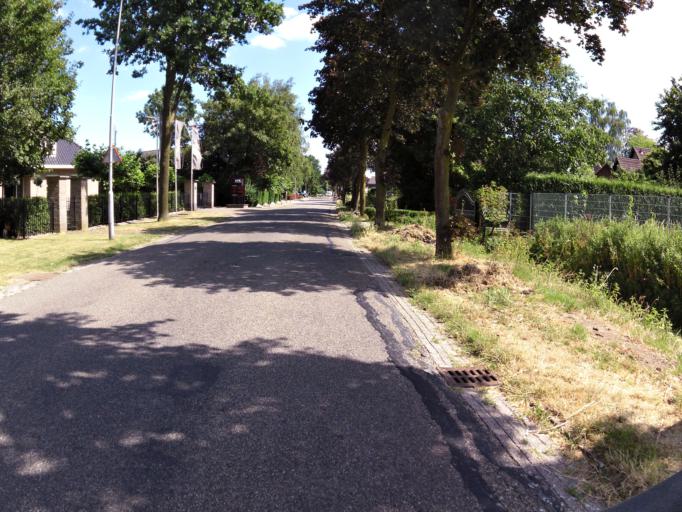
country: NL
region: Gelderland
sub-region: Gemeente Maasdriel
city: Hedel
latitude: 51.7526
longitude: 5.2605
